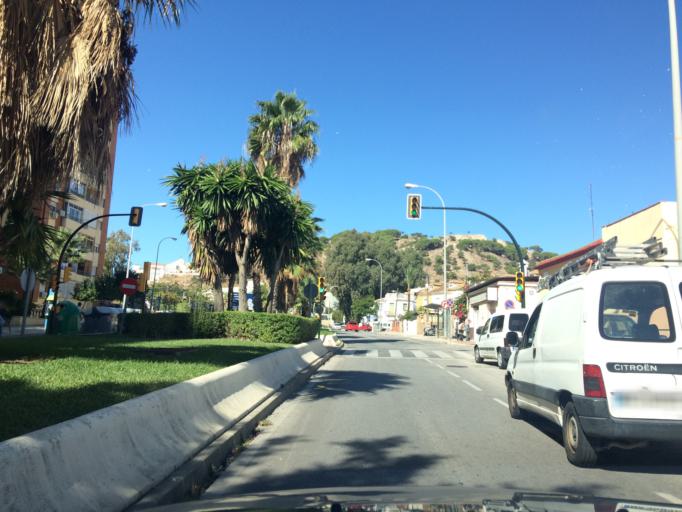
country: ES
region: Andalusia
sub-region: Provincia de Malaga
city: Malaga
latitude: 36.7313
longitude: -4.4362
